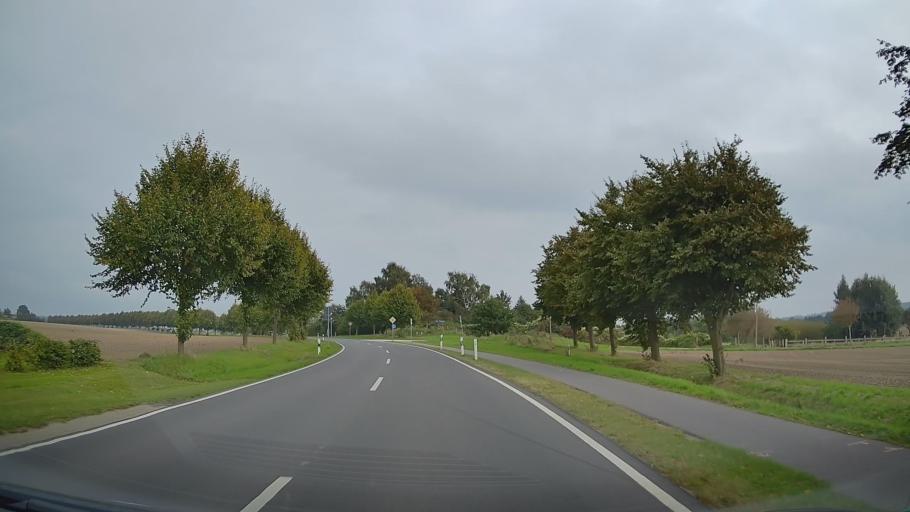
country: DE
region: Mecklenburg-Vorpommern
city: Ostseebad Kuhlungsborn
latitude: 54.1320
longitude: 11.7710
